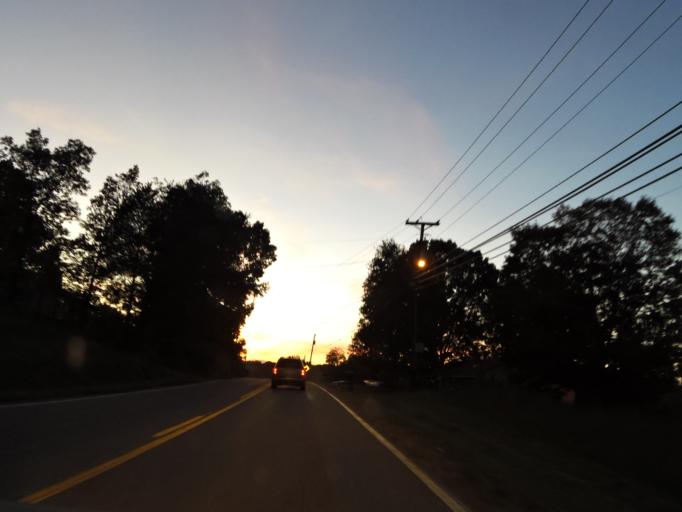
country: US
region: Tennessee
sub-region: Knox County
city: Mascot
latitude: 36.0208
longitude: -83.6509
